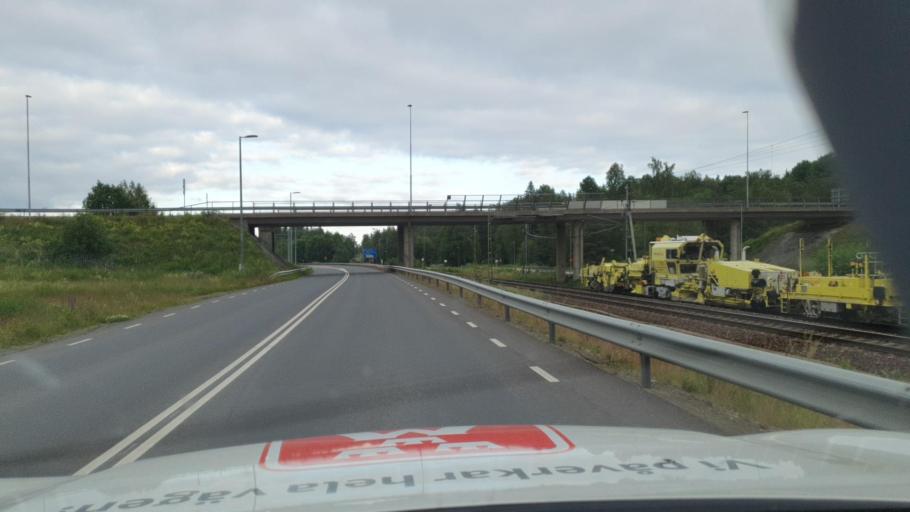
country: SE
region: Vaermland
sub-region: Karlstads Kommun
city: Karlstad
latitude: 59.4277
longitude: 13.4525
